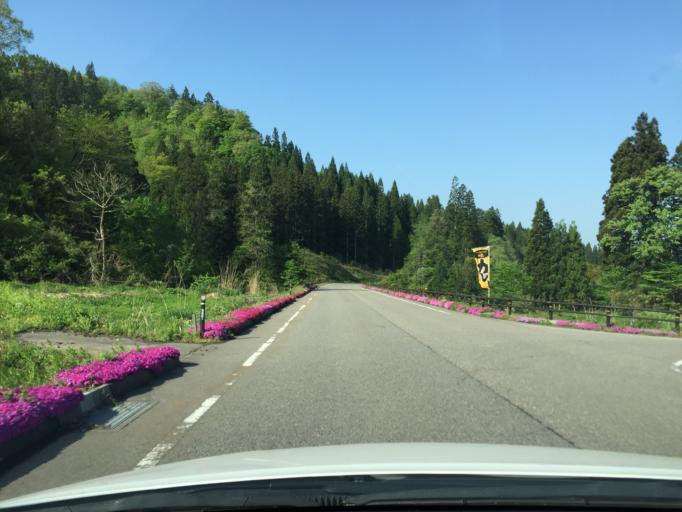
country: JP
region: Fukushima
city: Kitakata
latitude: 37.6866
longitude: 139.6719
